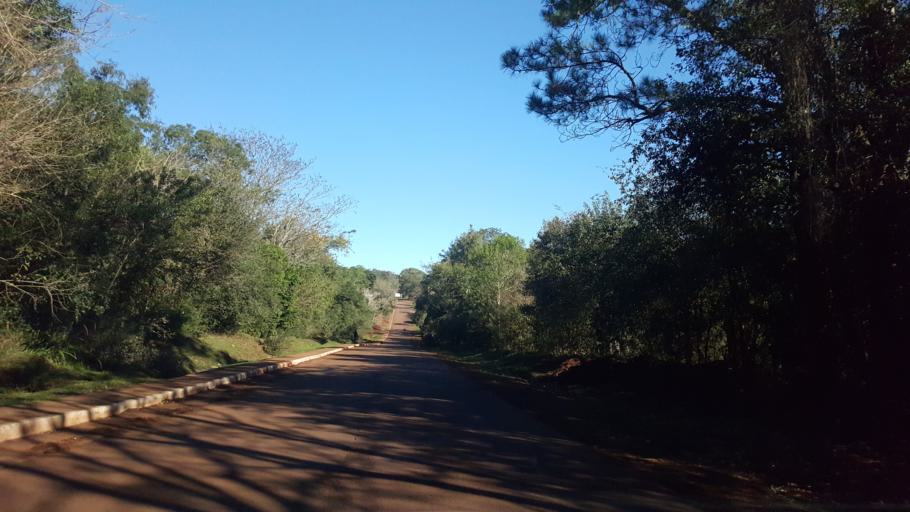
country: AR
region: Misiones
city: Jardin America
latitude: -27.0884
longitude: -55.2864
